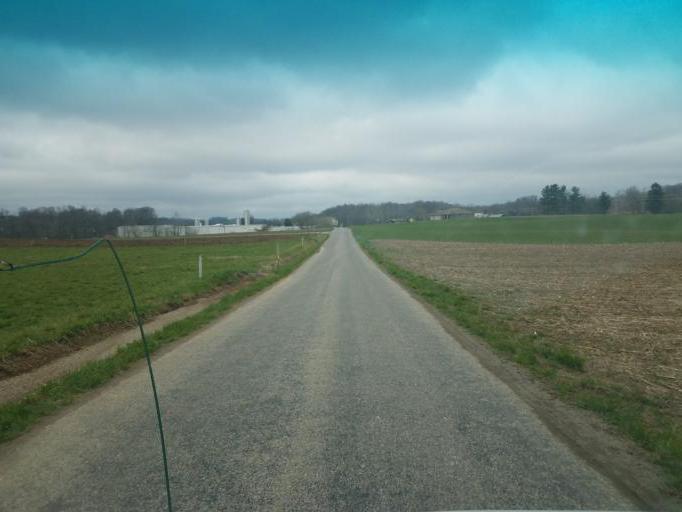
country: US
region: Ohio
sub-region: Stark County
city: Beach City
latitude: 40.6385
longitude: -81.6716
